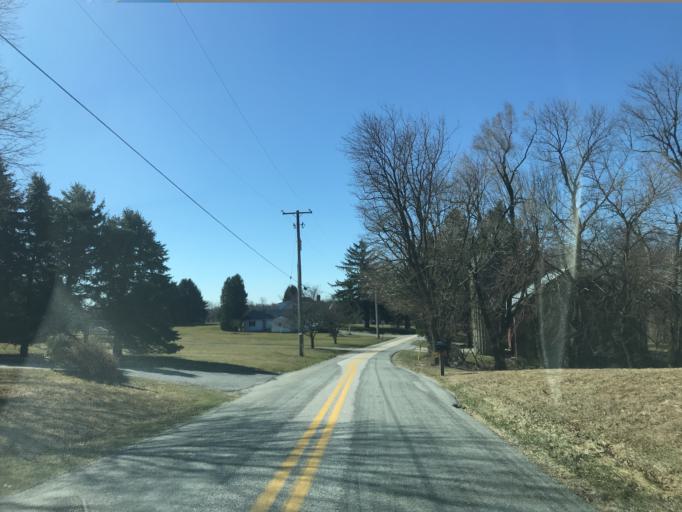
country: US
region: Pennsylvania
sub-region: York County
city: Stewartstown
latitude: 39.7229
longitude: -76.5228
